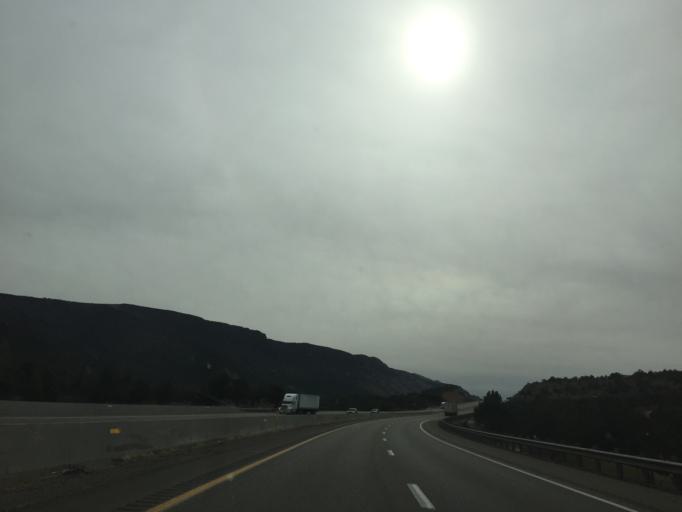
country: US
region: Utah
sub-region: Washington County
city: Toquerville
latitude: 37.4153
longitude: -113.2343
